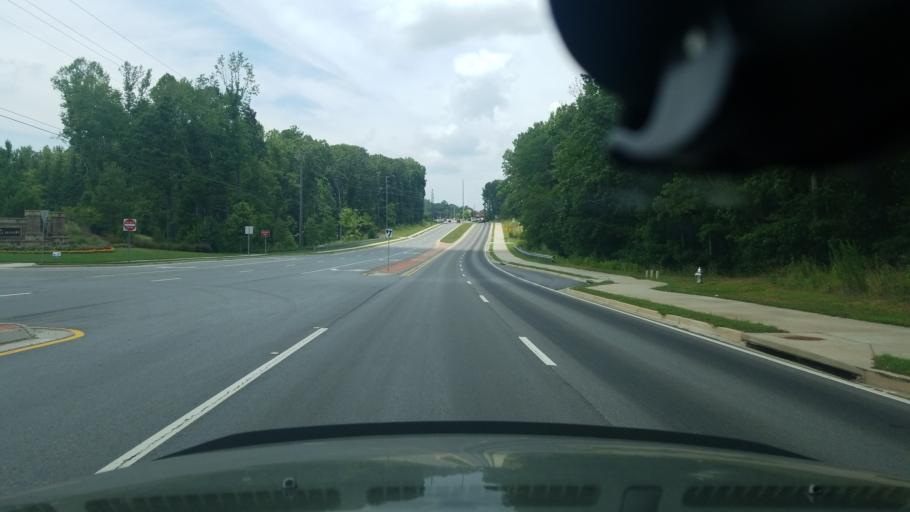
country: US
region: Georgia
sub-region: Fulton County
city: Milton
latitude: 34.1536
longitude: -84.2341
